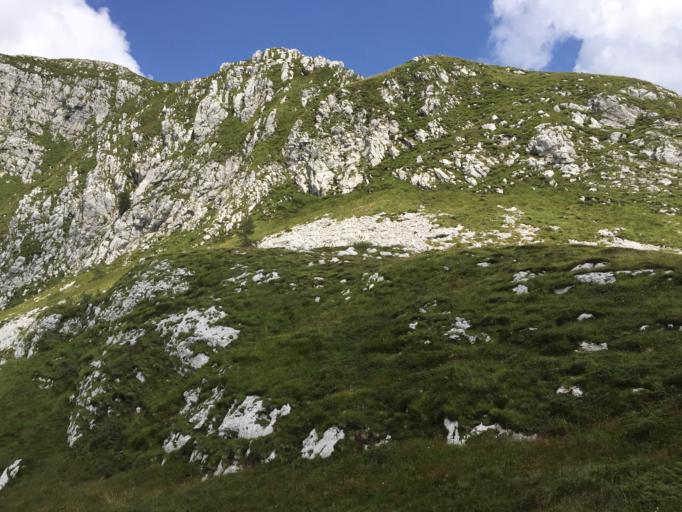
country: IT
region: Friuli Venezia Giulia
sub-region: Provincia di Pordenone
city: Budoia
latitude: 46.1192
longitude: 12.5069
